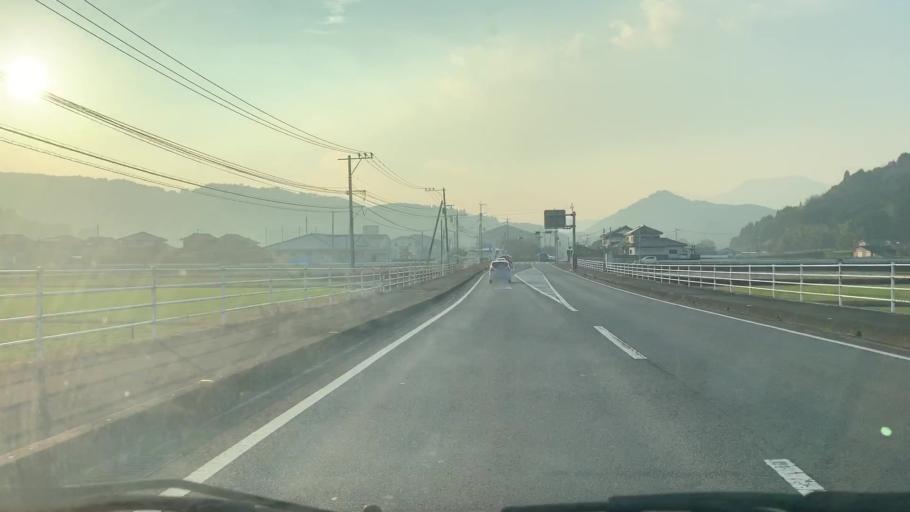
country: JP
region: Saga Prefecture
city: Takeocho-takeo
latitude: 33.2722
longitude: 130.1294
